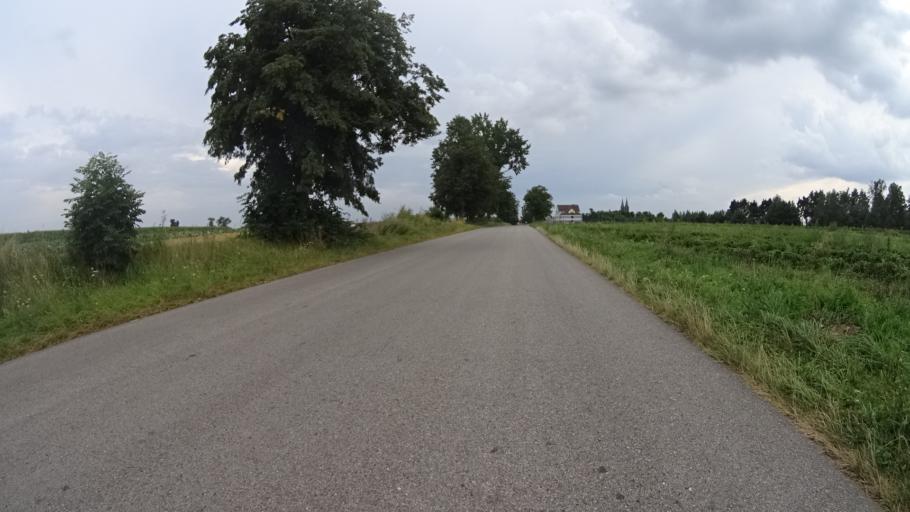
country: PL
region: Masovian Voivodeship
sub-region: Powiat bialobrzeski
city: Wysmierzyce
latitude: 51.6689
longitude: 20.8565
